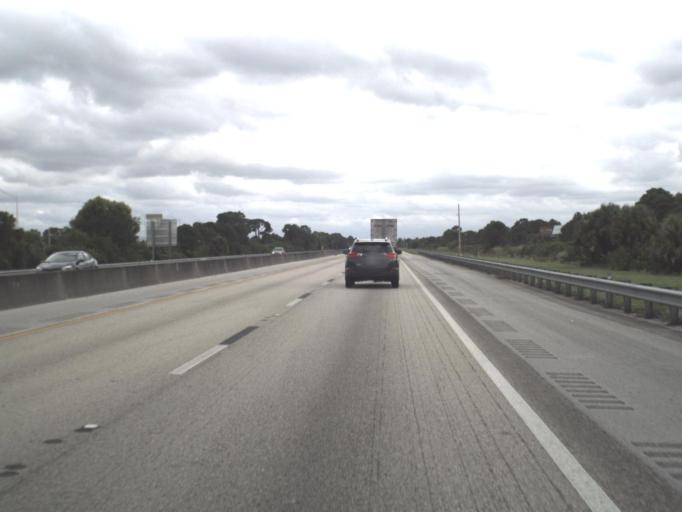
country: US
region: Florida
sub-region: Palm Beach County
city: Limestone Creek
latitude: 26.9107
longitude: -80.1433
